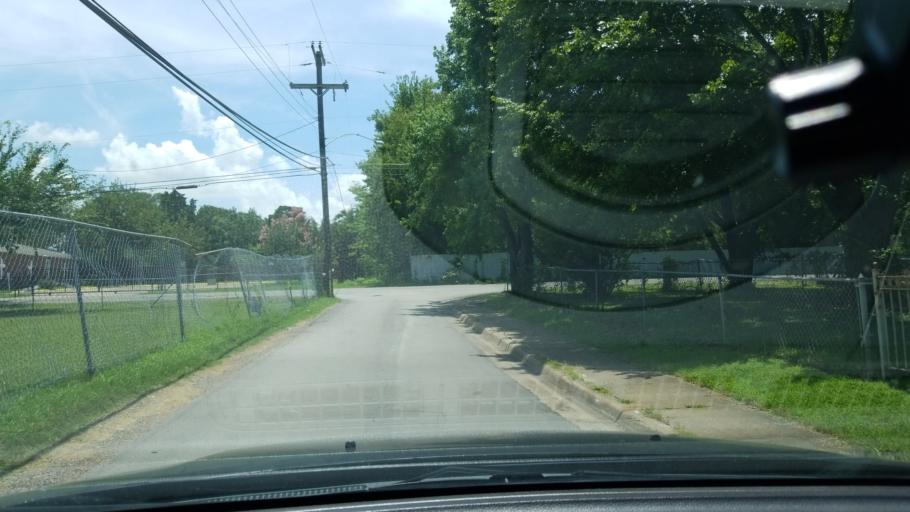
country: US
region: Texas
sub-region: Dallas County
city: Balch Springs
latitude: 32.7518
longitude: -96.6494
